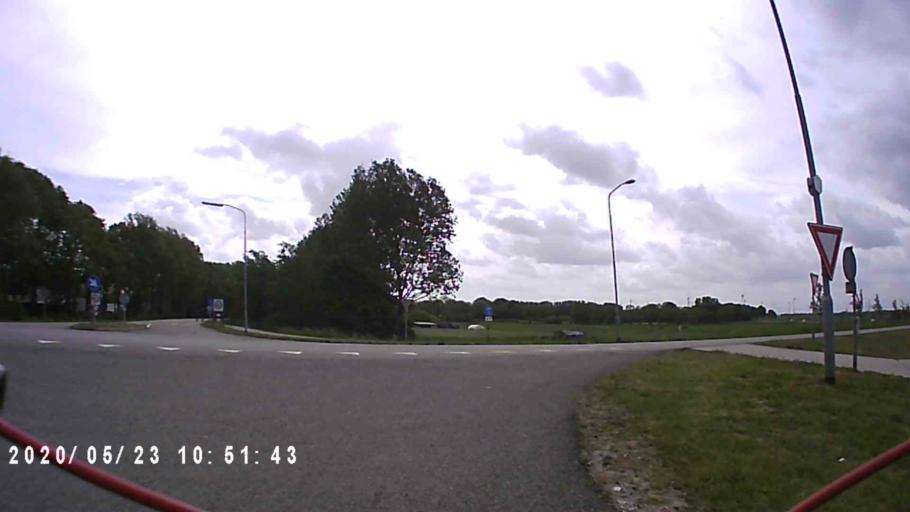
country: NL
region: Groningen
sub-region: Gemeente Delfzijl
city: Delfzijl
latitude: 53.3139
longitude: 6.9413
